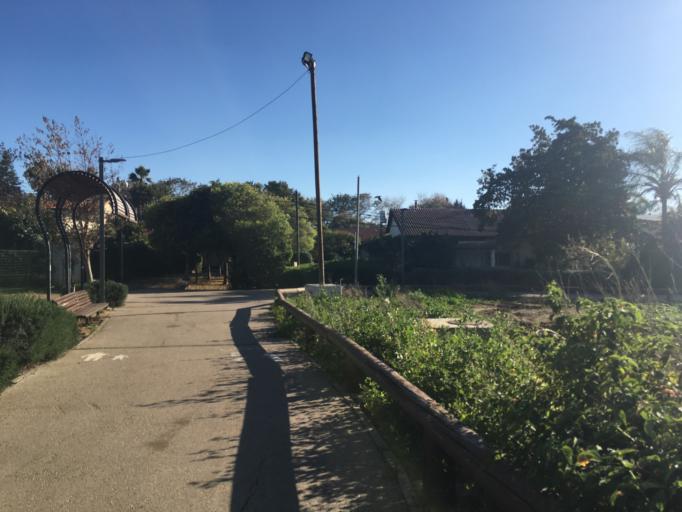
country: IL
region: Tel Aviv
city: Ramat HaSharon
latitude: 32.1421
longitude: 34.8256
